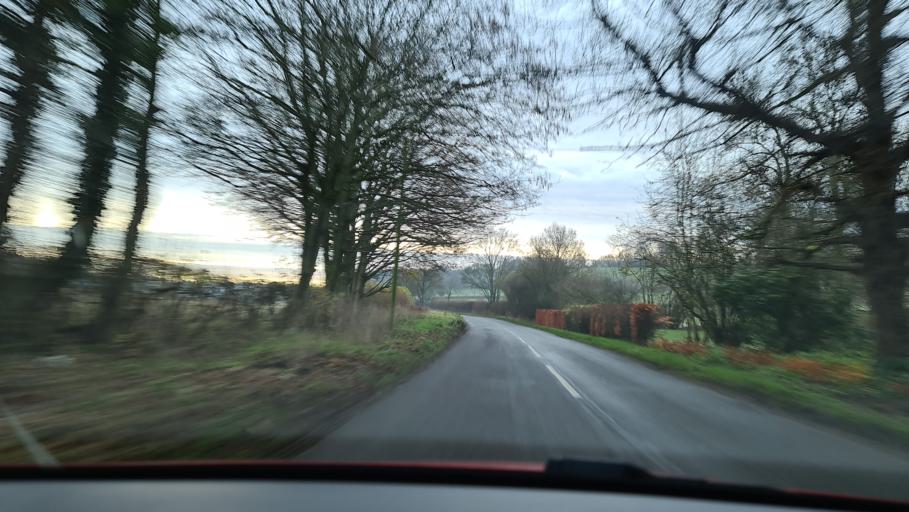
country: GB
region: England
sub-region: Buckinghamshire
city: Great Missenden
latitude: 51.7122
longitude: -0.7464
